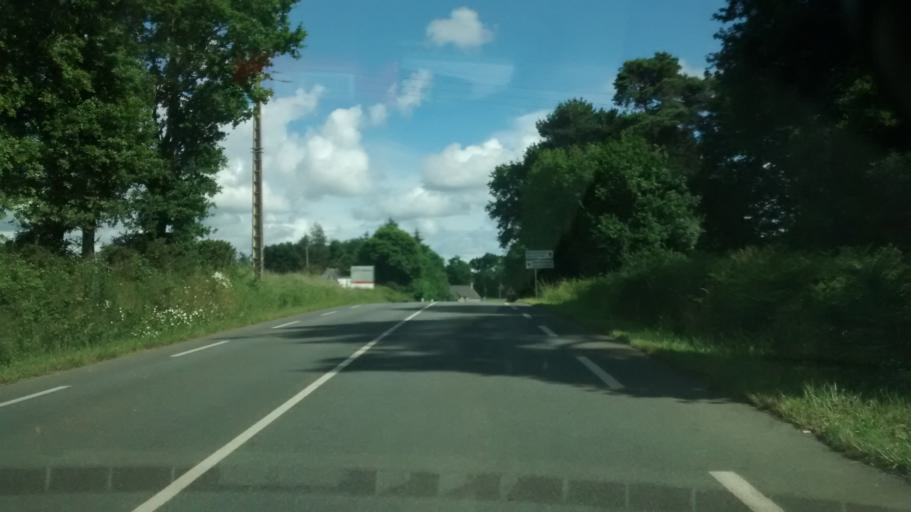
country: FR
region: Brittany
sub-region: Departement du Morbihan
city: Malestroit
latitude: 47.8284
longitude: -2.3825
